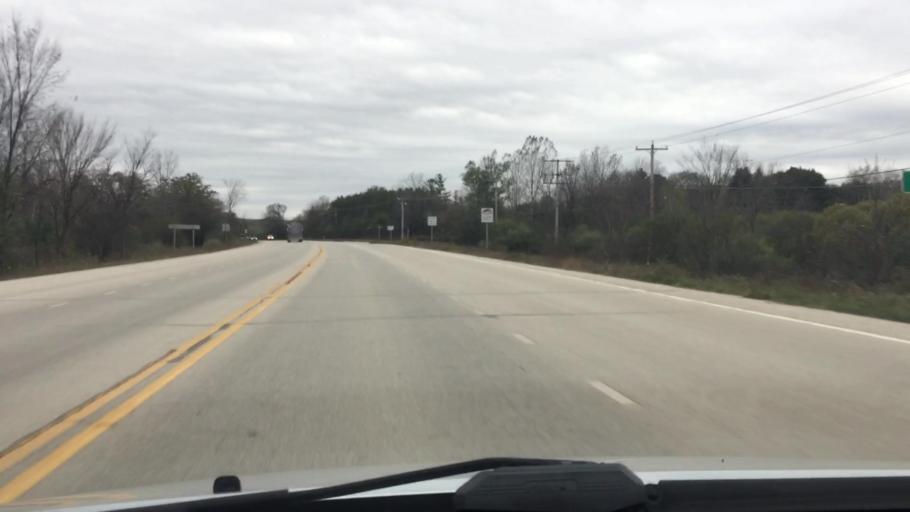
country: US
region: Wisconsin
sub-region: Waukesha County
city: Wales
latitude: 42.9731
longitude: -88.3039
